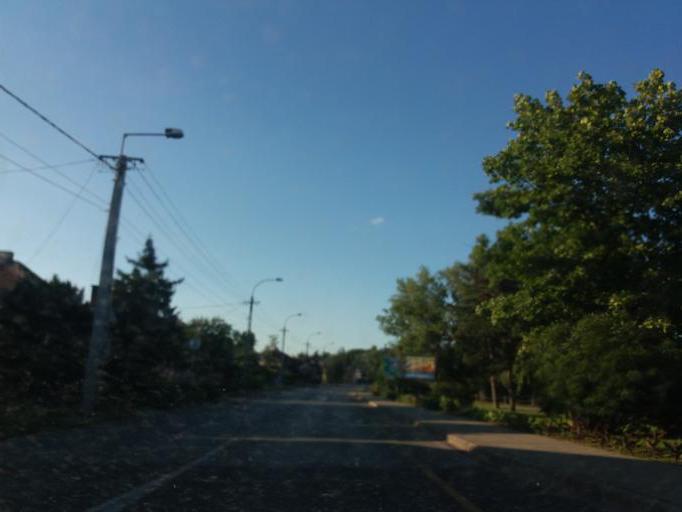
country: HU
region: Fejer
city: Martonvasar
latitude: 47.3114
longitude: 18.7873
